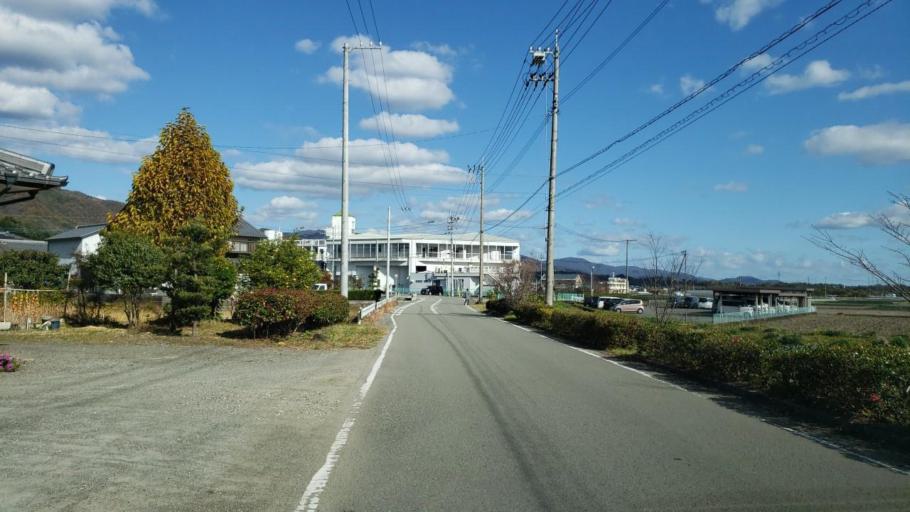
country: JP
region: Tokushima
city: Wakimachi
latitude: 34.0747
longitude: 134.1932
